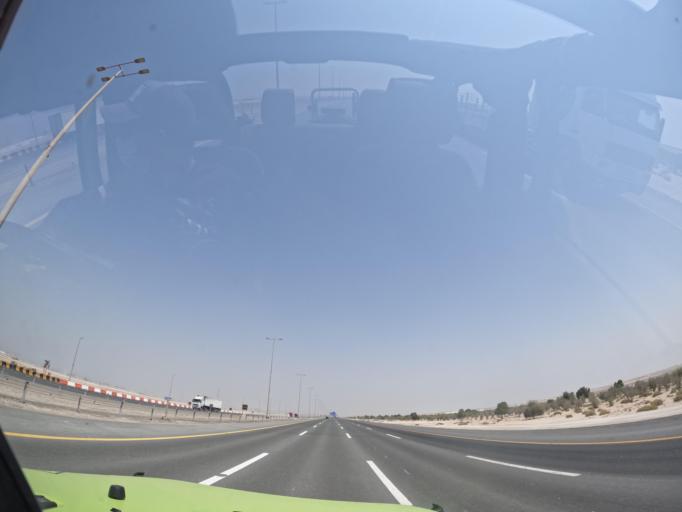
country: AE
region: Abu Dhabi
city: Abu Dhabi
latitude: 24.2718
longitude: 54.5064
